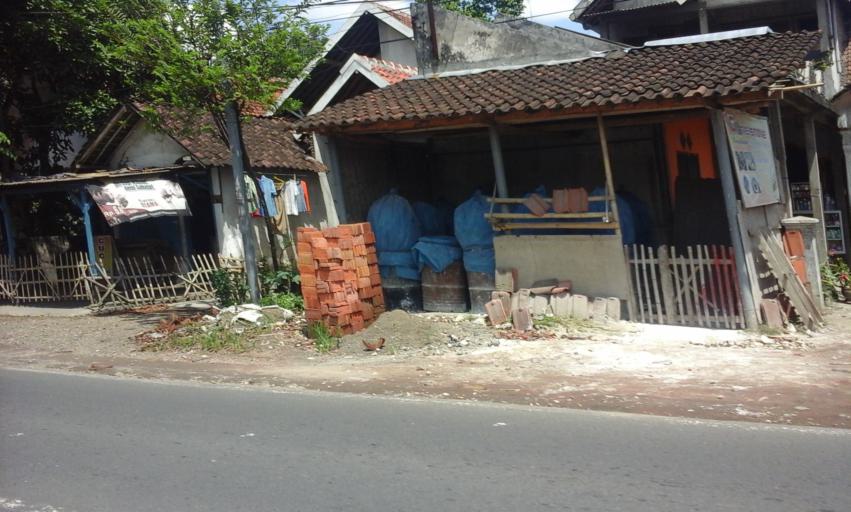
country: ID
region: East Java
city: Kertosari
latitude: -8.1880
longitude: 113.7529
